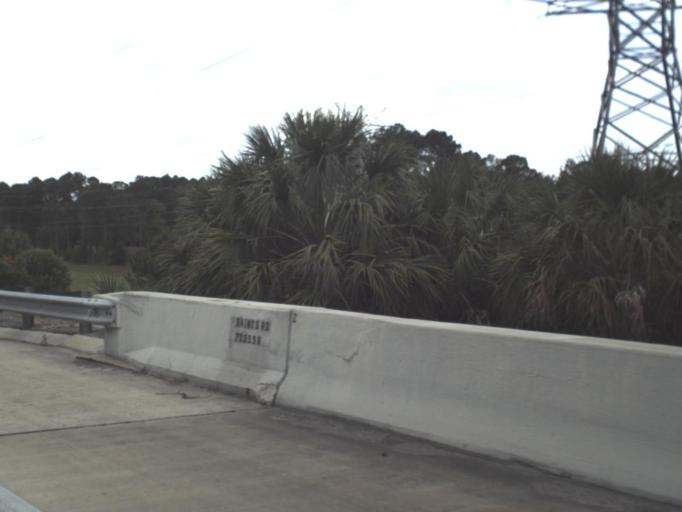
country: US
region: Florida
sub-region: Duval County
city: Neptune Beach
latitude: 30.2948
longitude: -81.5221
